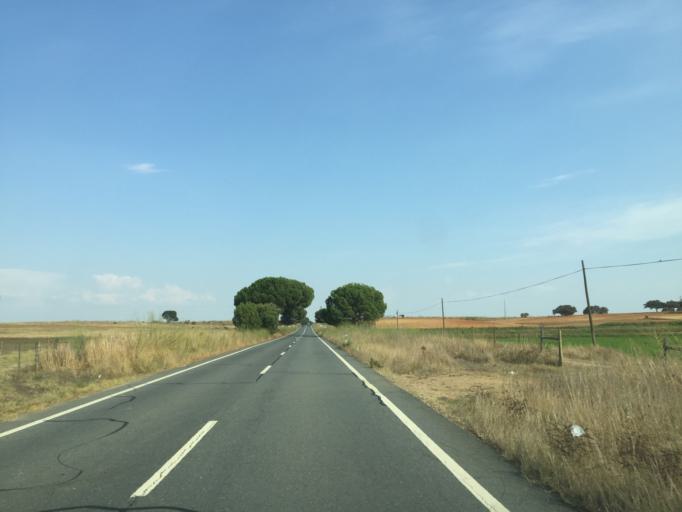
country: PT
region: Beja
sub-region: Aljustrel
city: Aljustrel
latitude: 37.9320
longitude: -8.3489
